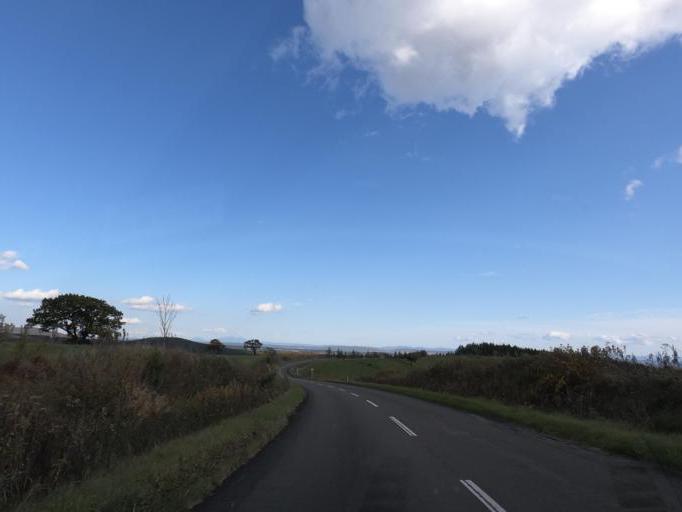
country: JP
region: Hokkaido
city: Otofuke
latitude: 43.2772
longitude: 143.2308
